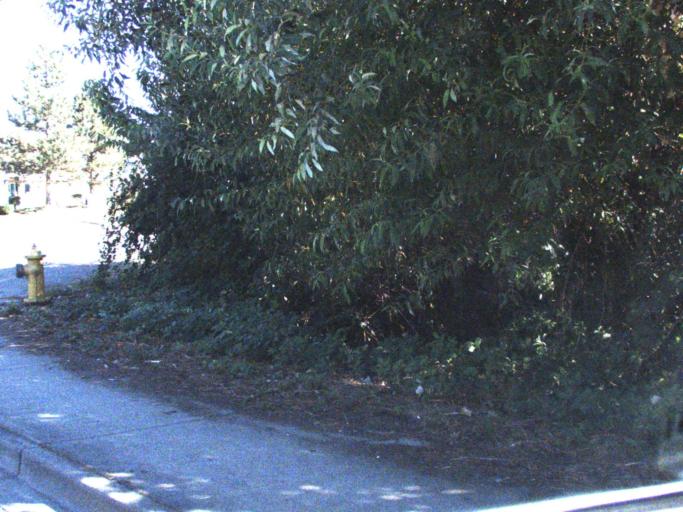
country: US
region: Washington
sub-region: King County
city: Renton
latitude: 47.4709
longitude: -122.2078
